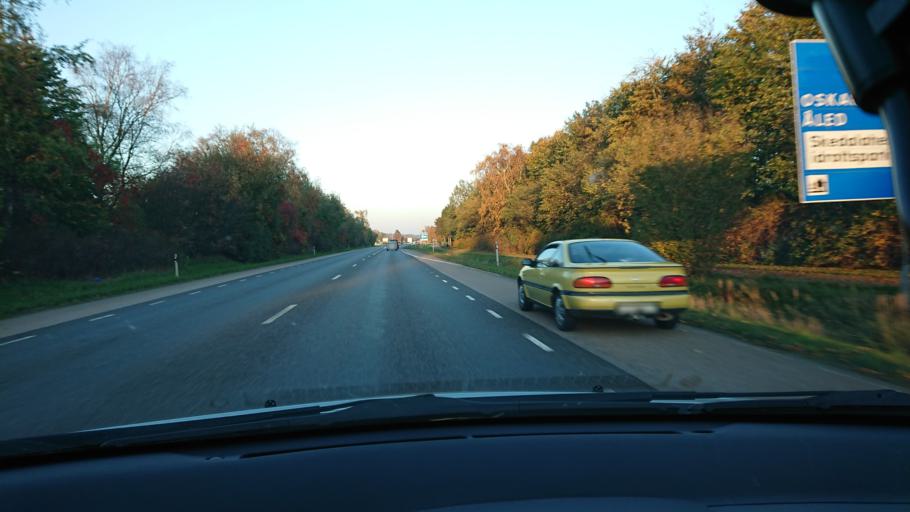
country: SE
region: Halland
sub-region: Halmstads Kommun
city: Fyllinge
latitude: 56.6840
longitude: 12.9431
